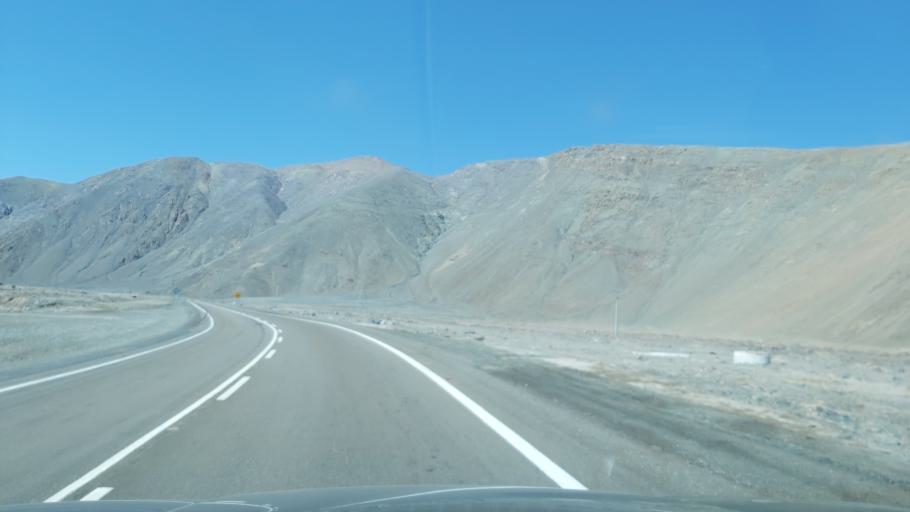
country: CL
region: Atacama
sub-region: Provincia de Chanaral
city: Diego de Almagro
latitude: -26.3399
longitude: -69.7460
